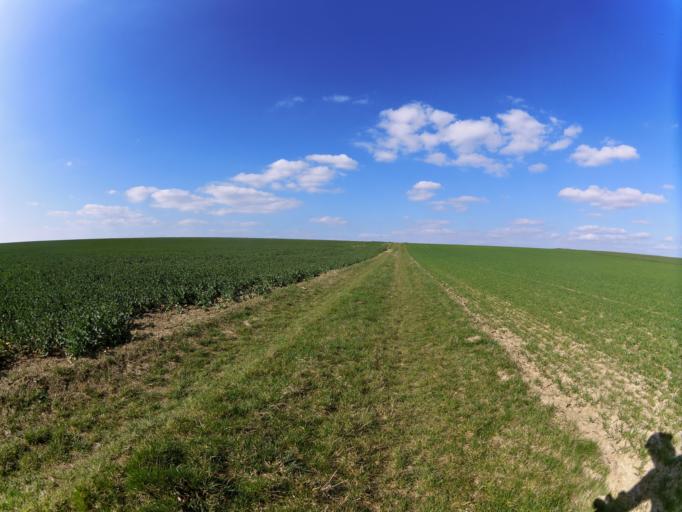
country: DE
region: Bavaria
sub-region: Regierungsbezirk Unterfranken
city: Dettelbach
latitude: 49.8349
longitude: 10.1612
